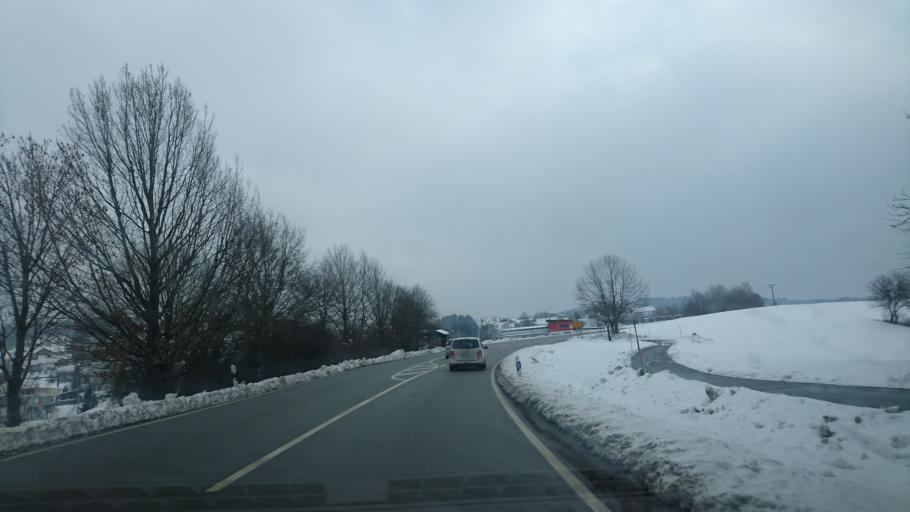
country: DE
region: Bavaria
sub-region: Lower Bavaria
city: Aussernzell
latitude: 48.6829
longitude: 13.1871
